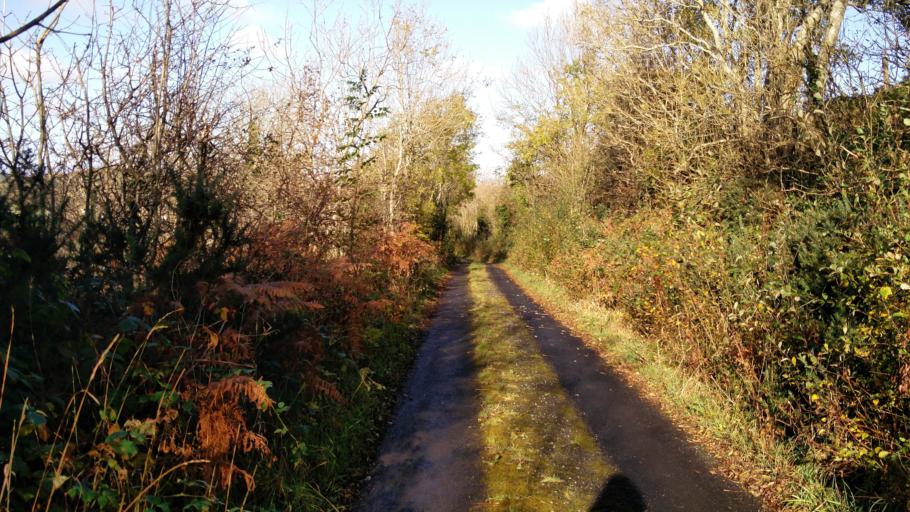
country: IE
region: Connaught
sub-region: Maigh Eo
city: Westport
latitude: 53.7819
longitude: -9.4562
